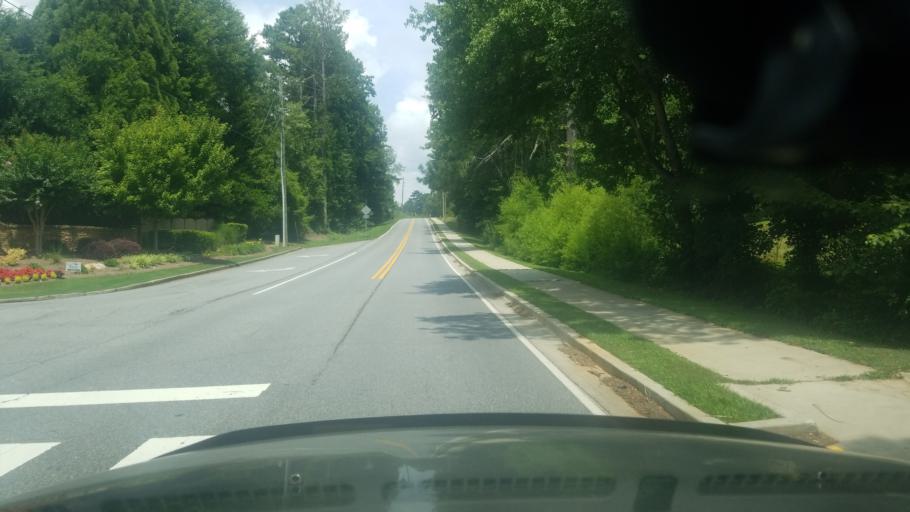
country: US
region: Georgia
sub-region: Fulton County
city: Johns Creek
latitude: 34.0974
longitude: -84.1852
